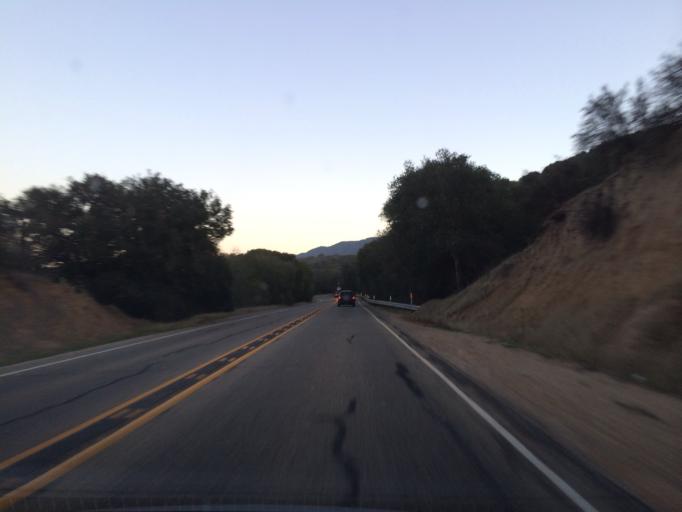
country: US
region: California
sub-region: Santa Barbara County
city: Santa Ynez
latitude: 34.5813
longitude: -119.9898
